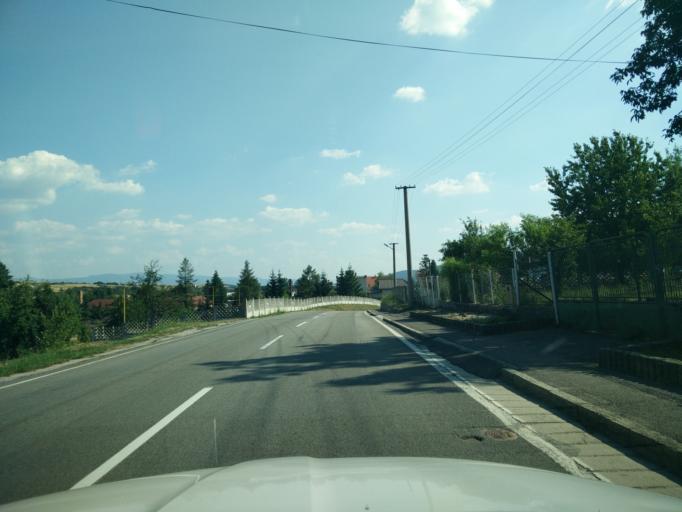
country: SK
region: Nitriansky
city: Bojnice
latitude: 48.8273
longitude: 18.4782
